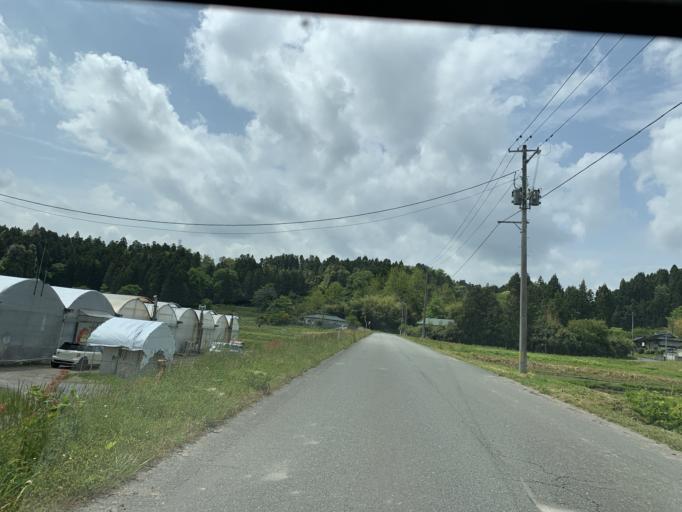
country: JP
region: Miyagi
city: Furukawa
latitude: 38.7397
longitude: 140.9307
